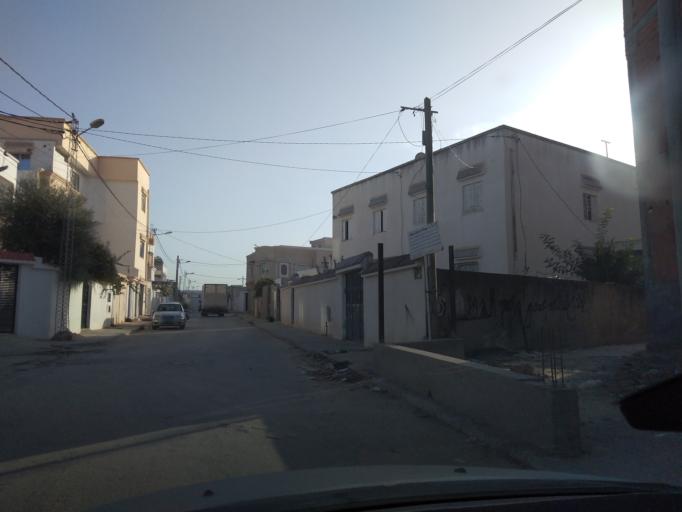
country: TN
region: Manouba
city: Manouba
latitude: 36.7912
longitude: 10.0879
